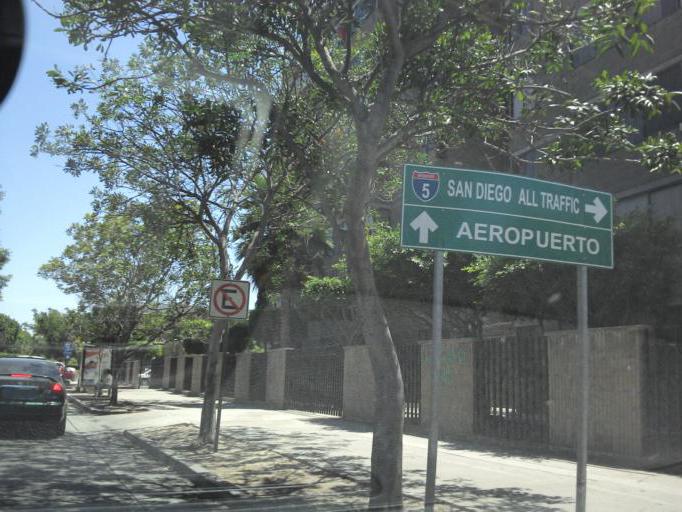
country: MX
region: Baja California
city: Tijuana
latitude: 32.5338
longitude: -117.0199
